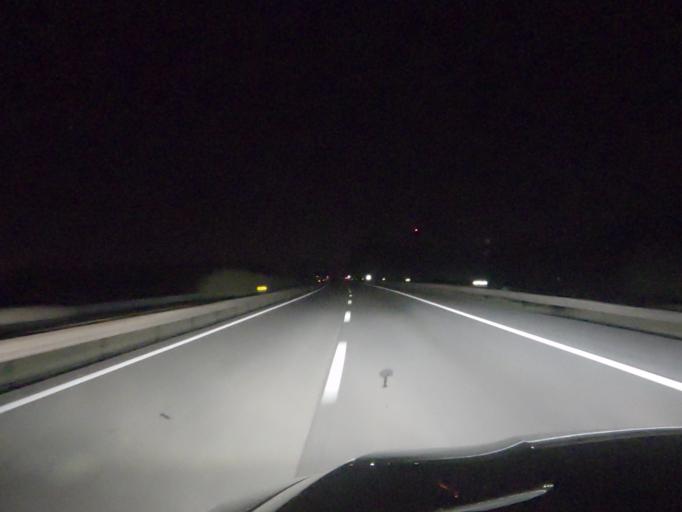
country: PT
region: Aveiro
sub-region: Albergaria-A-Velha
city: Albergaria-a-Velha
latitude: 40.7113
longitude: -8.5216
